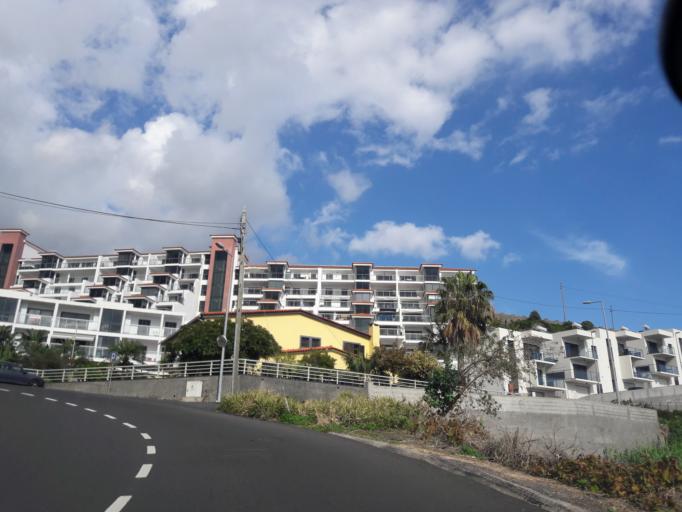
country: PT
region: Madeira
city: Canico
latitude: 32.6448
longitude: -16.8333
